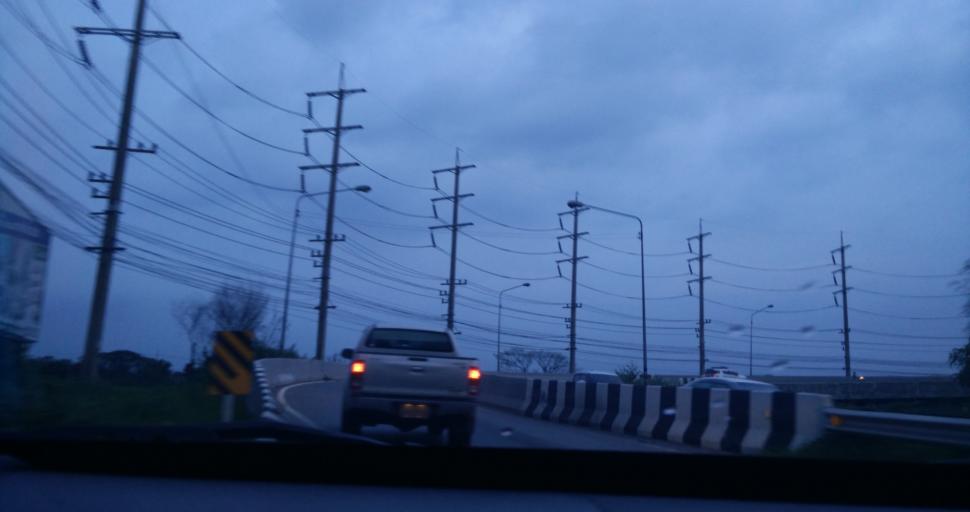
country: TH
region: Phra Nakhon Si Ayutthaya
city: Ban Bang Kadi Pathum Thani
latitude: 13.9962
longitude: 100.6153
